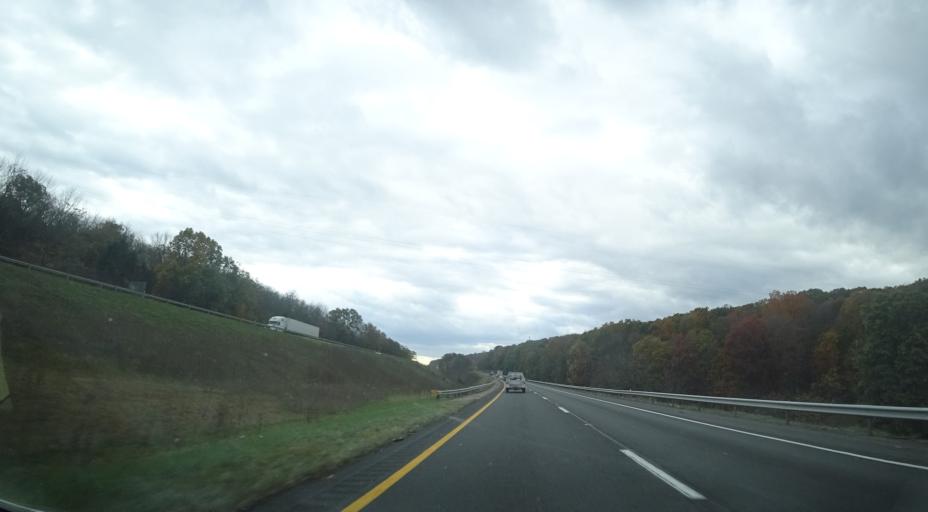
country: US
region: Virginia
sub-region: Shenandoah County
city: New Market
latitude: 38.6287
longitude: -78.6969
